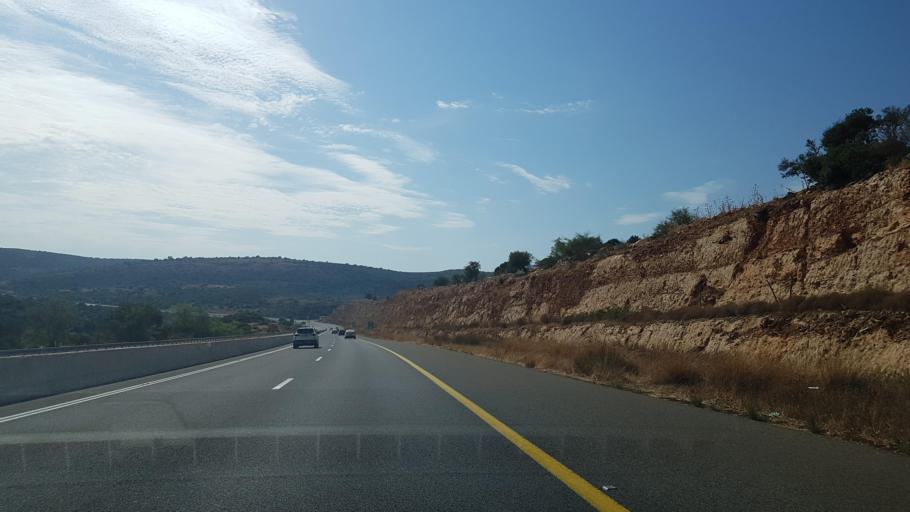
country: IL
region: Northern District
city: Maghar
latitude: 32.8712
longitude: 35.4638
